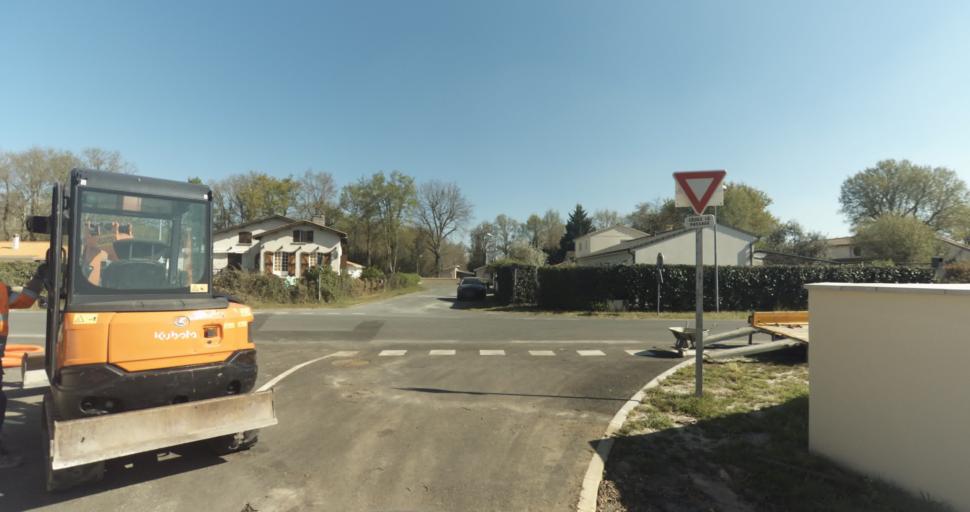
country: FR
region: Aquitaine
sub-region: Departement de la Gironde
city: Martignas-sur-Jalle
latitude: 44.8042
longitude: -0.7941
